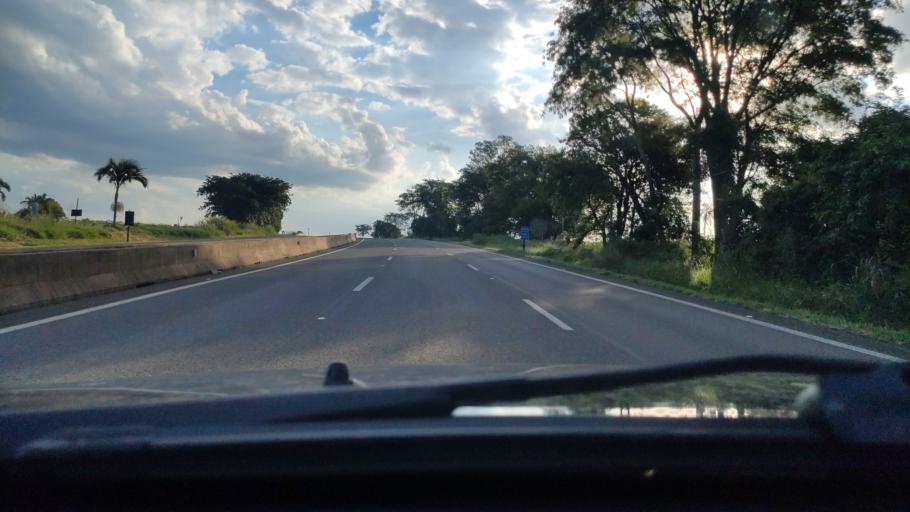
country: BR
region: Sao Paulo
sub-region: Mogi-Mirim
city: Mogi Mirim
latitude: -22.4507
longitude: -47.0828
